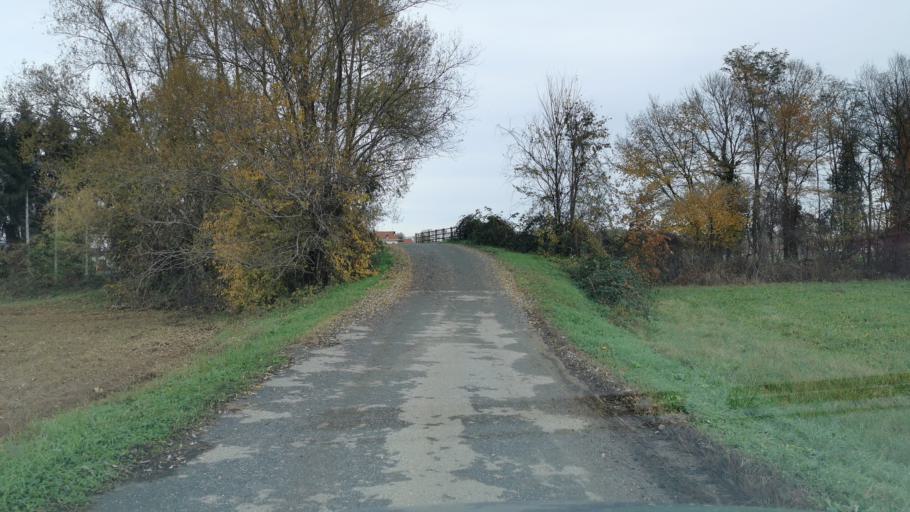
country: IT
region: Piedmont
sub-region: Provincia di Torino
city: San Francesco al Campo
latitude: 45.2127
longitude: 7.6773
